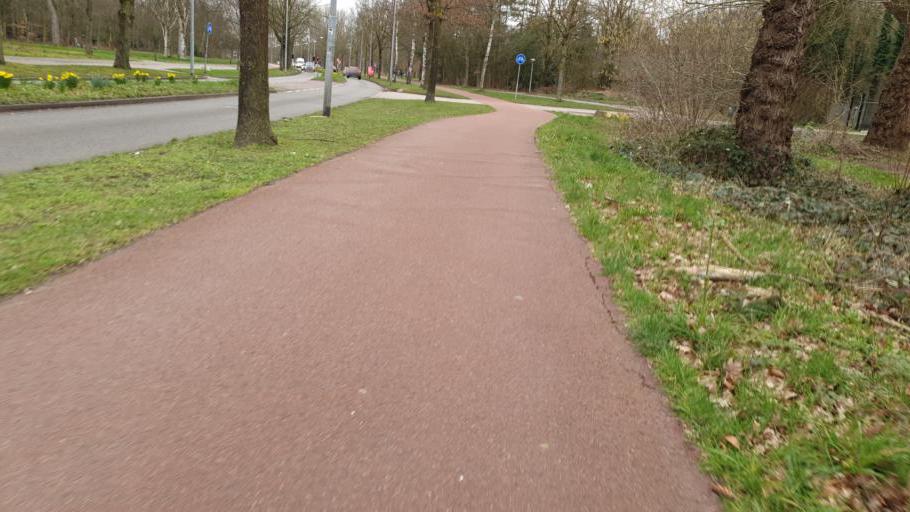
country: NL
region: North Brabant
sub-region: Gemeente Eindhoven
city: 't Hofke
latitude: 51.4575
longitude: 5.5049
